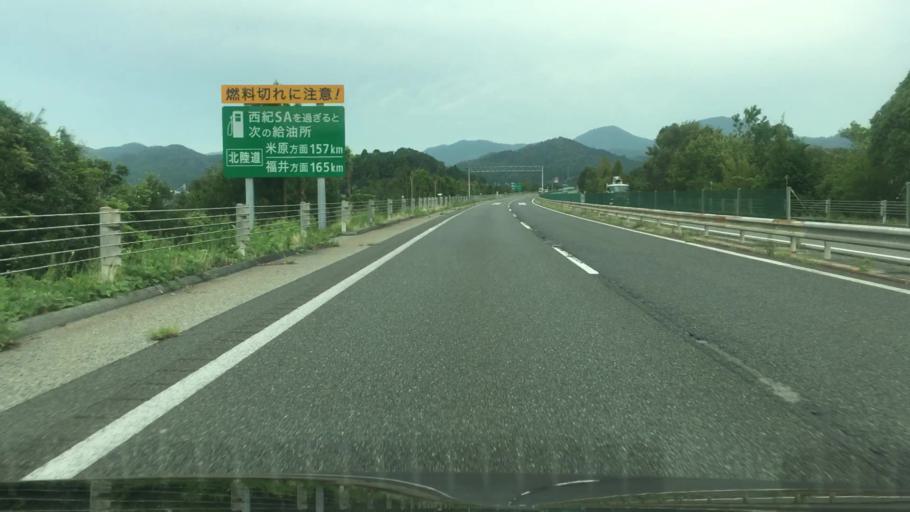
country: JP
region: Hyogo
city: Sasayama
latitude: 35.0723
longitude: 135.1729
